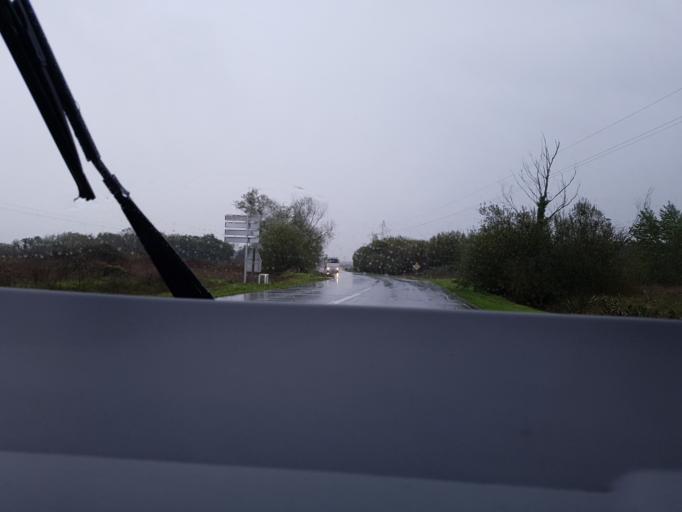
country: FR
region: Aquitaine
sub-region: Departement de la Gironde
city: Bassens
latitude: 44.9247
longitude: -0.5294
